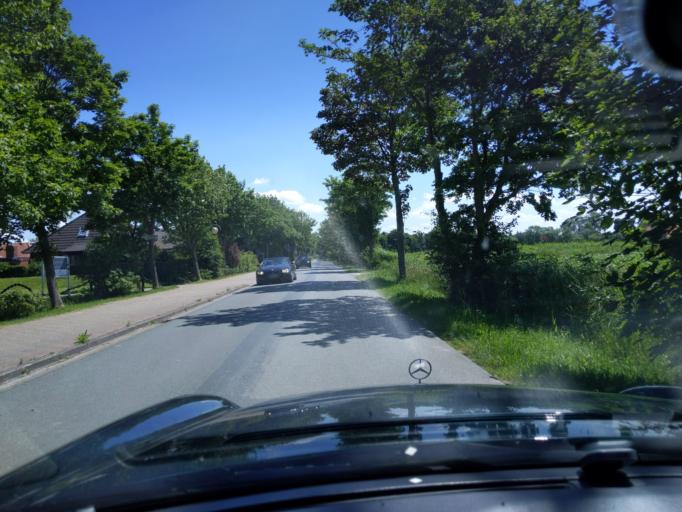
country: DE
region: Lower Saxony
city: Butjadingen
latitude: 53.5732
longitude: 8.2561
